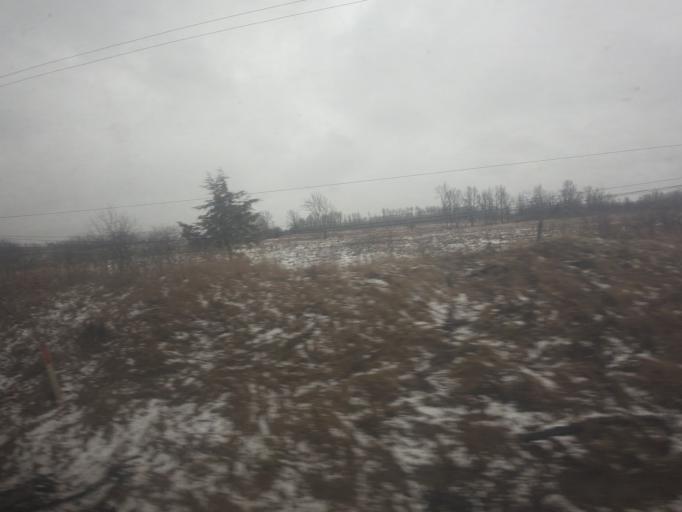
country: CA
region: Ontario
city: Deseronto
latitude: 44.2215
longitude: -77.1397
